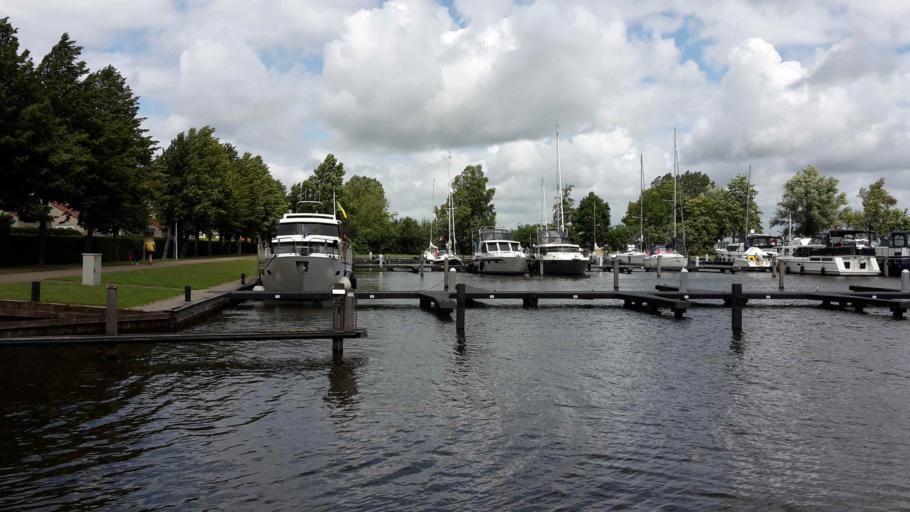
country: NL
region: Friesland
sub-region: Gemeente Skarsterlan
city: Sint Nicolaasga
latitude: 52.9607
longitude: 5.7215
